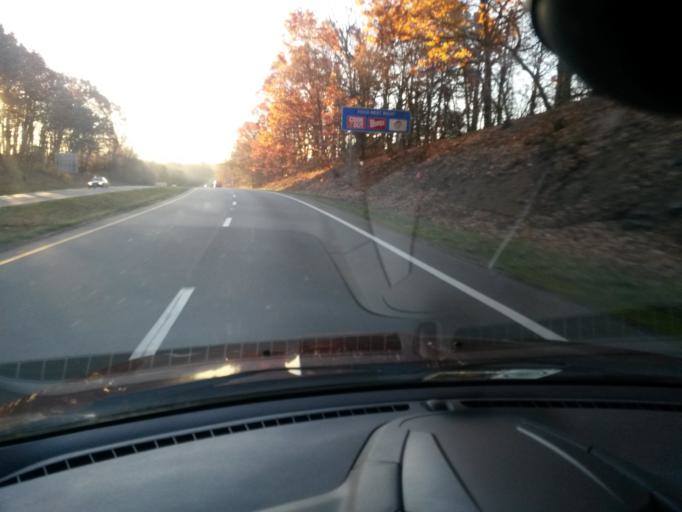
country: US
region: Virginia
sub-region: Franklin County
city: Rocky Mount
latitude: 37.0188
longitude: -79.8813
